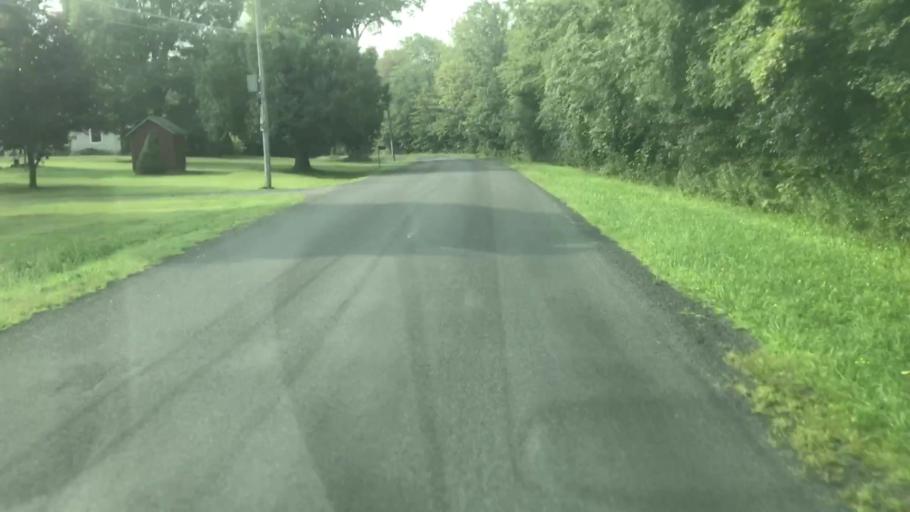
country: US
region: New York
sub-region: Onondaga County
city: Skaneateles
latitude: 42.9139
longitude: -76.4562
